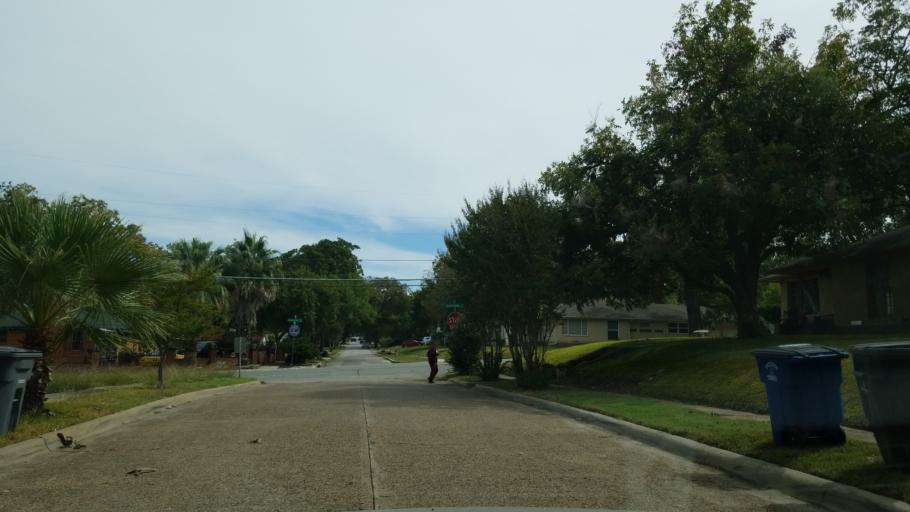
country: US
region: Texas
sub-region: Dallas County
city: Dallas
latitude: 32.7751
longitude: -96.7184
